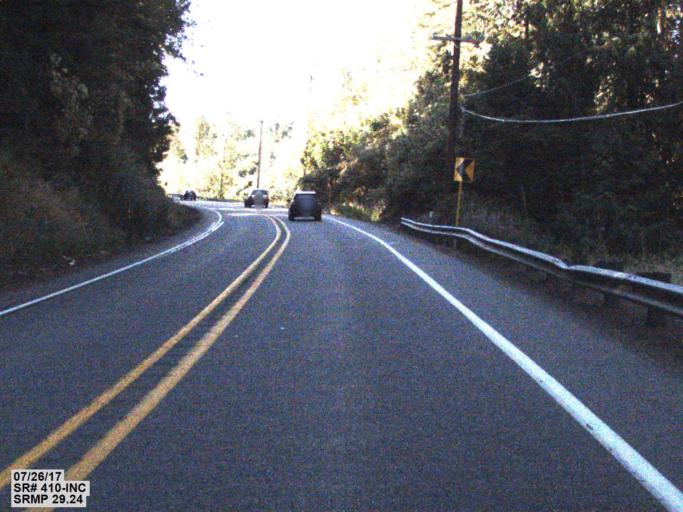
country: US
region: Washington
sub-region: King County
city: Enumclaw
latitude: 47.1670
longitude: -121.9121
